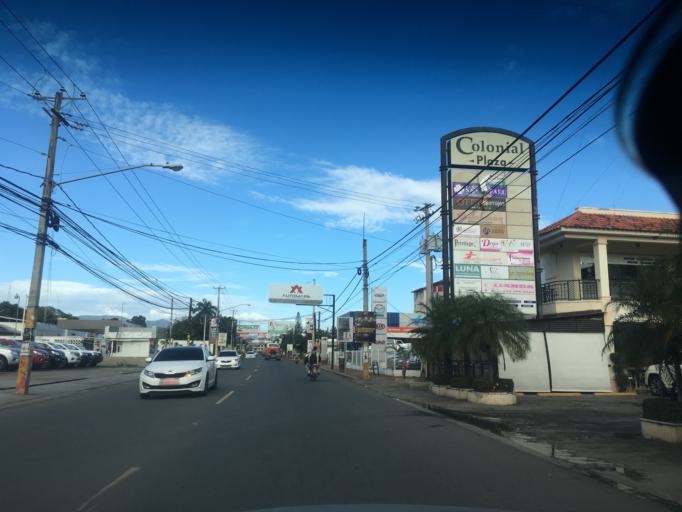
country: DO
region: Duarte
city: San Francisco de Macoris
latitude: 19.2883
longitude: -70.2662
